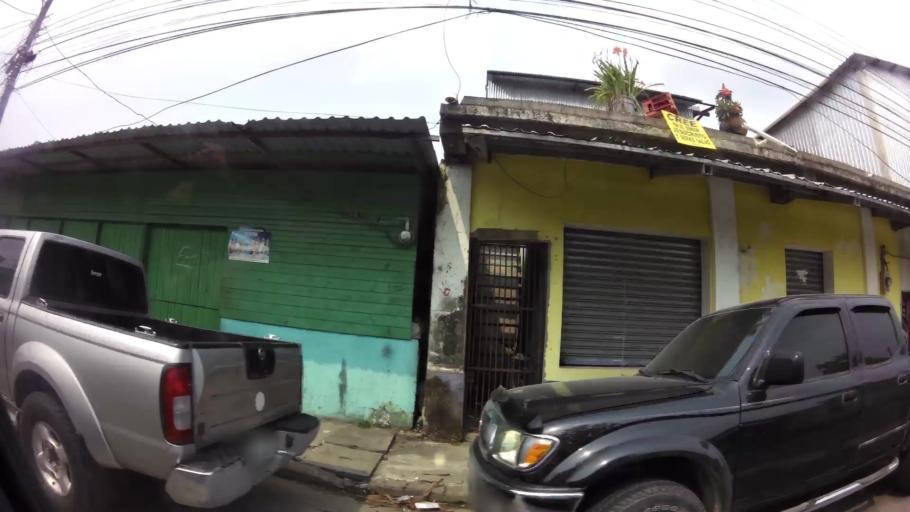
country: HN
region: Atlantida
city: Tela
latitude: 15.7826
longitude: -87.4530
